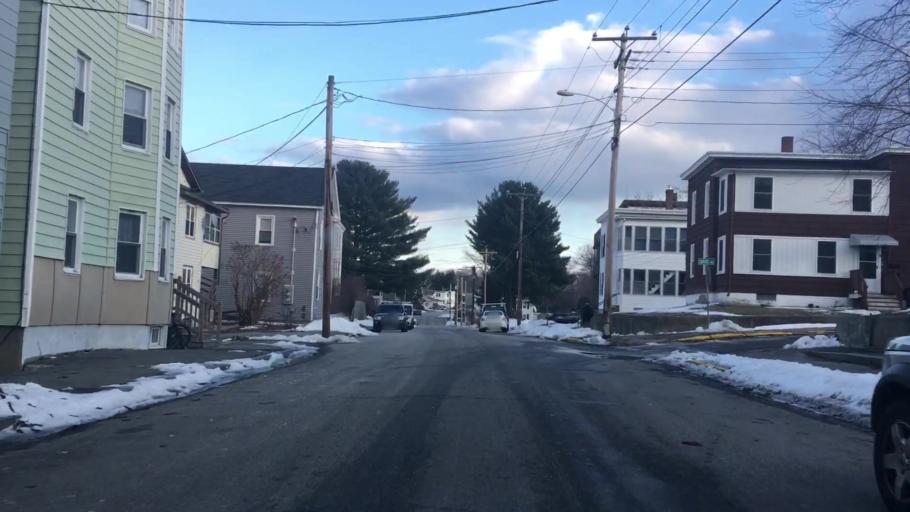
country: US
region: Maine
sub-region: York County
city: Saco
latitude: 43.4896
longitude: -70.4425
